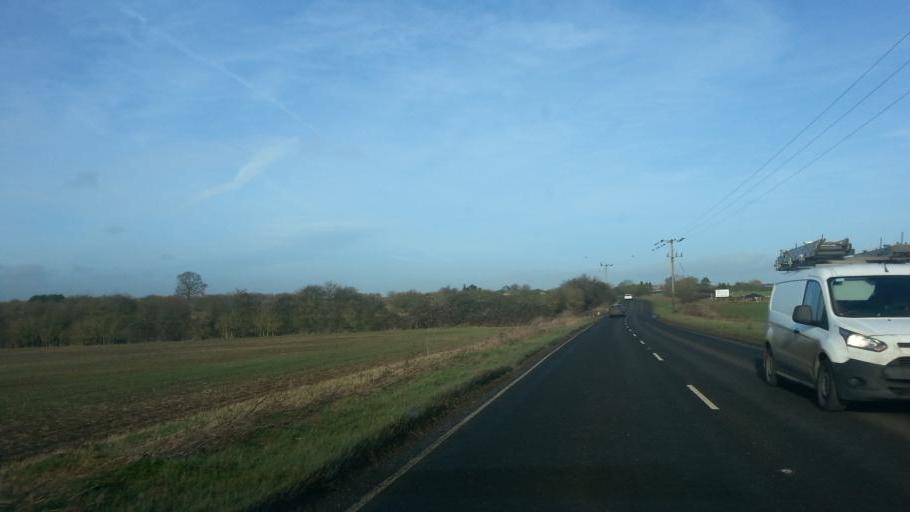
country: GB
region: England
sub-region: Cambridgeshire
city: Warboys
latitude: 52.4110
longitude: -0.1025
